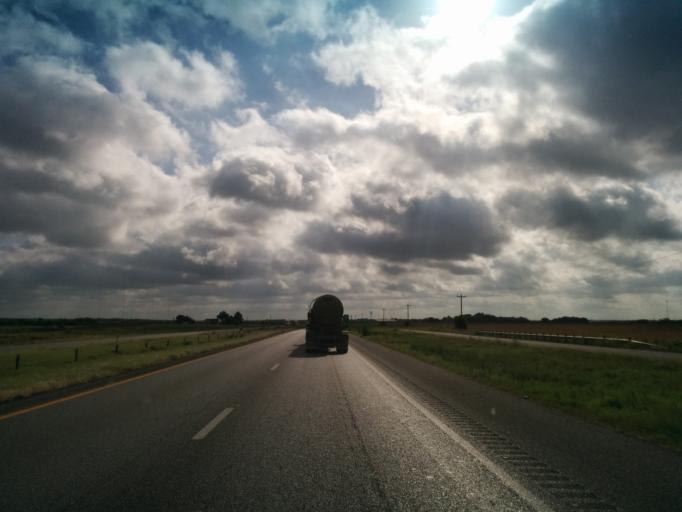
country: US
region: Texas
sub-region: Guadalupe County
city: Marion
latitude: 29.5213
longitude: -98.1326
